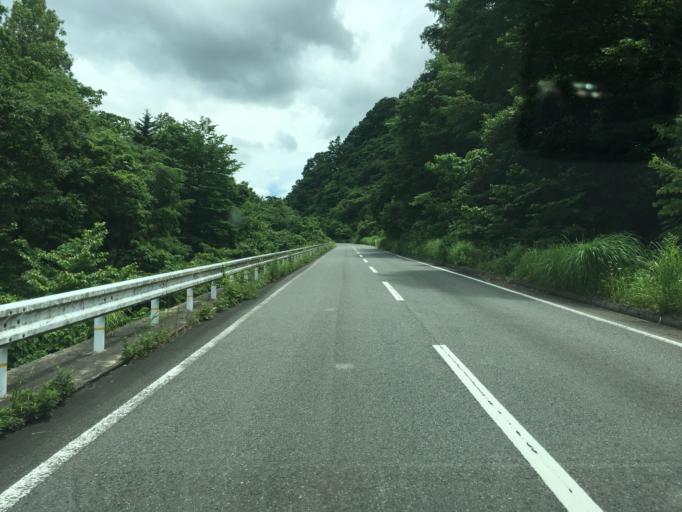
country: JP
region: Miyagi
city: Marumori
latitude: 37.7078
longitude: 140.8775
